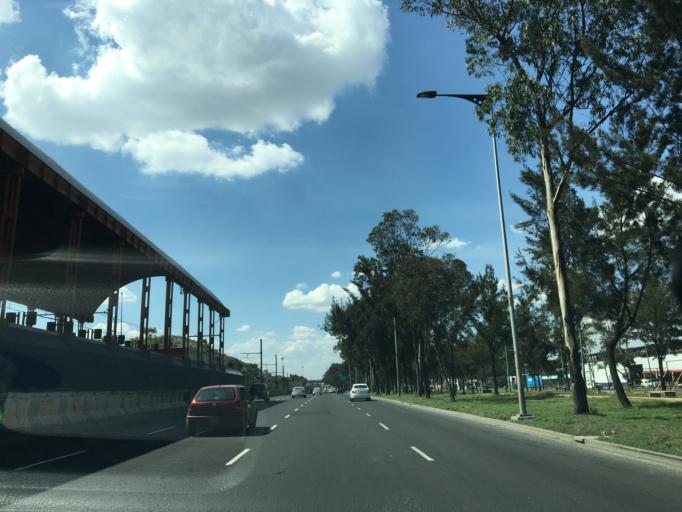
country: MX
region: Mexico
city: Ciudad Nezahualcoyotl
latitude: 19.3735
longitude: -99.0170
